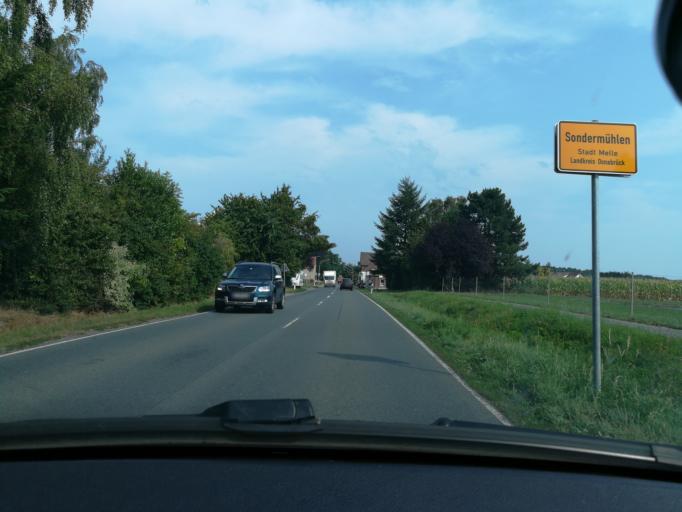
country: DE
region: Lower Saxony
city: Melle
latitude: 52.1636
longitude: 8.3331
